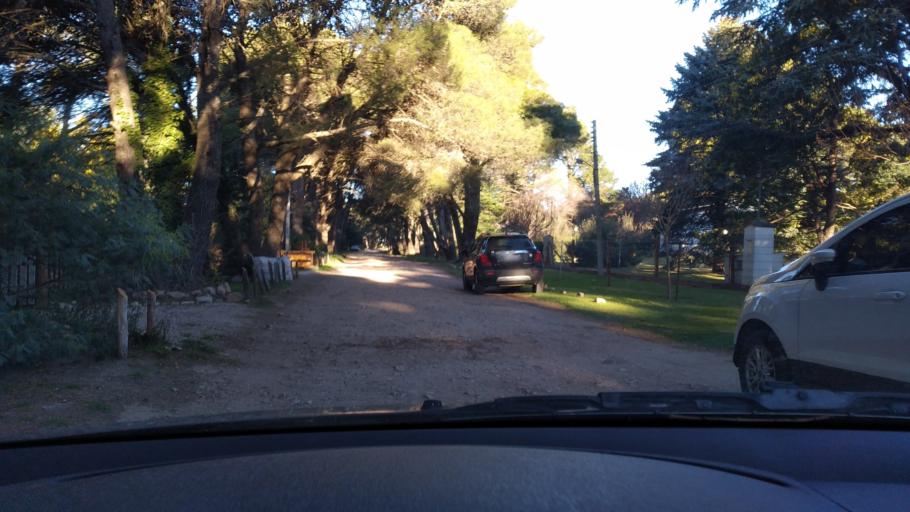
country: AR
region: Buenos Aires
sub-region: Partido de Tornquist
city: Tornquist
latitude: -38.0830
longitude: -61.9346
